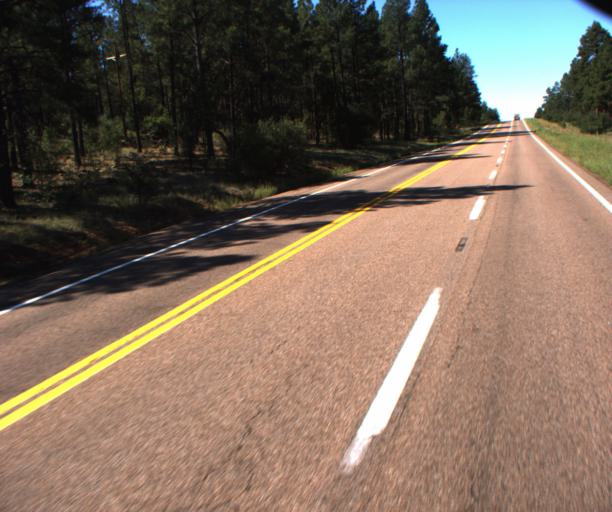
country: US
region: Arizona
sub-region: Navajo County
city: Linden
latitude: 34.0940
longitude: -110.1728
